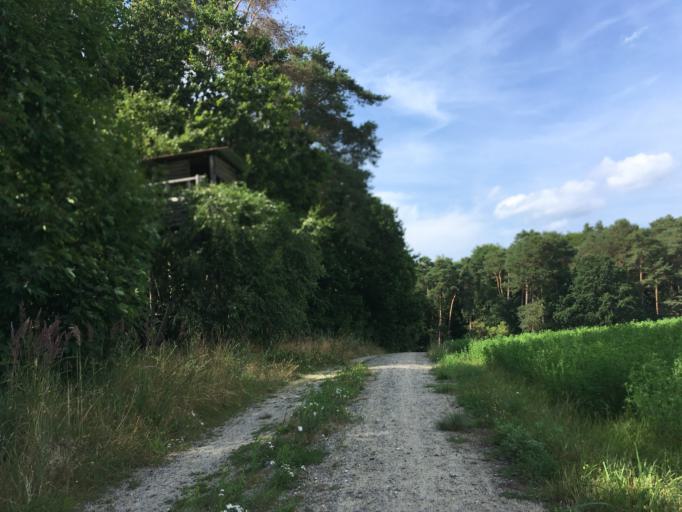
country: DE
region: Brandenburg
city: Rudnitz
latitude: 52.7488
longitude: 13.5755
